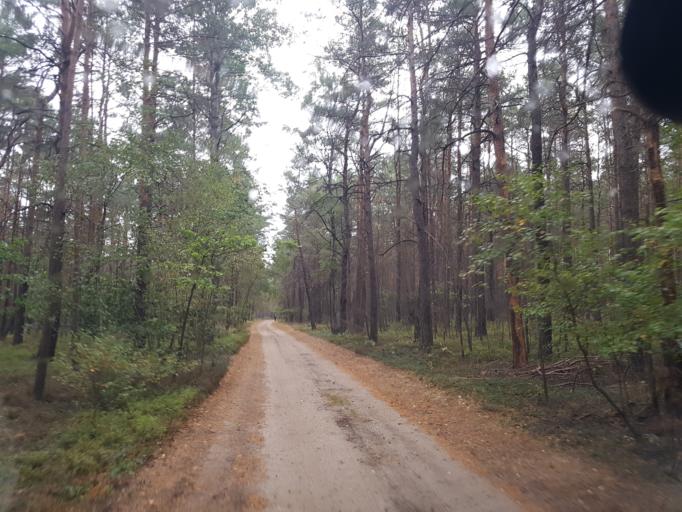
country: DE
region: Brandenburg
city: Sallgast
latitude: 51.6115
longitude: 13.7786
